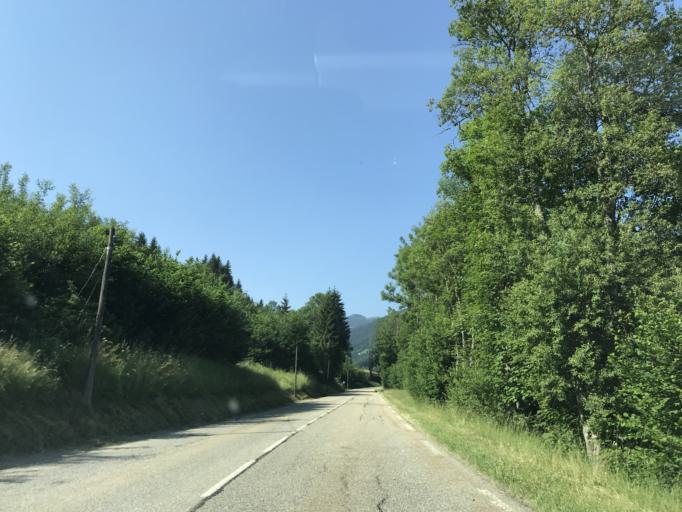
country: FR
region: Rhone-Alpes
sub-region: Departement de l'Isere
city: Allevard
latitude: 45.3253
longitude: 6.0899
